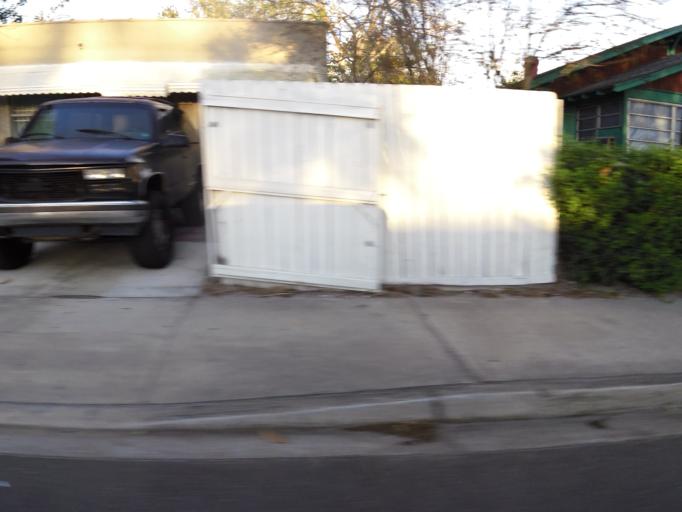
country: US
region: Florida
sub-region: Duval County
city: Jacksonville
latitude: 30.3269
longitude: -81.7055
